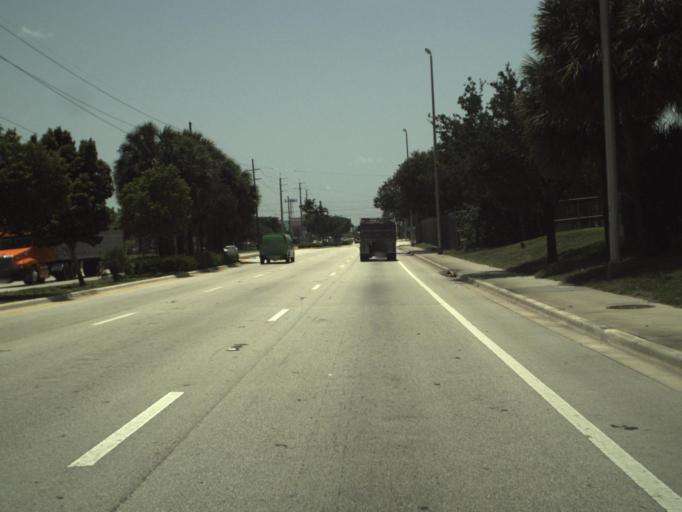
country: US
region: Florida
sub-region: Broward County
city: Coconut Creek
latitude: 26.2641
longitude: -80.1521
